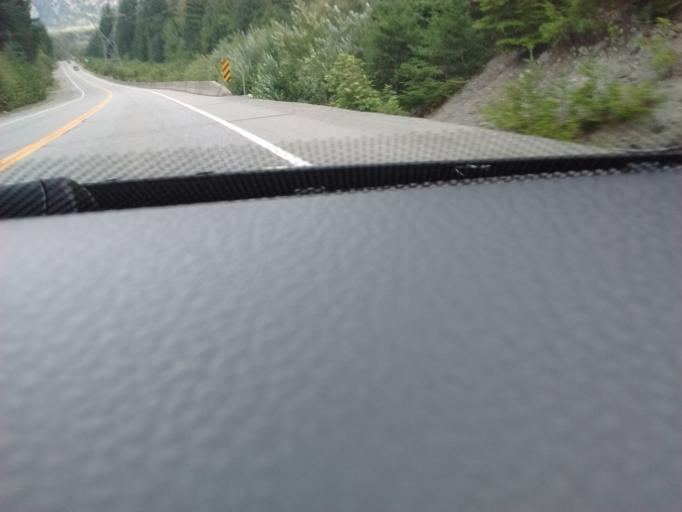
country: CA
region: British Columbia
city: Pemberton
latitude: 50.3025
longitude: -122.8104
